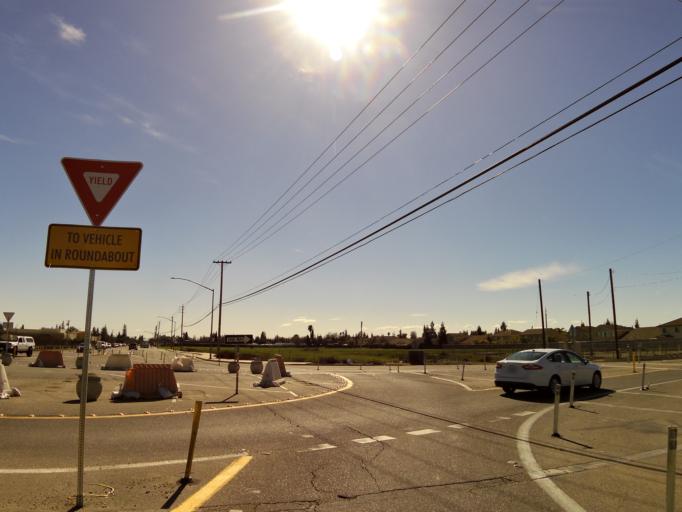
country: US
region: California
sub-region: Stanislaus County
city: Riverbank
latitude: 37.7001
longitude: -120.9765
